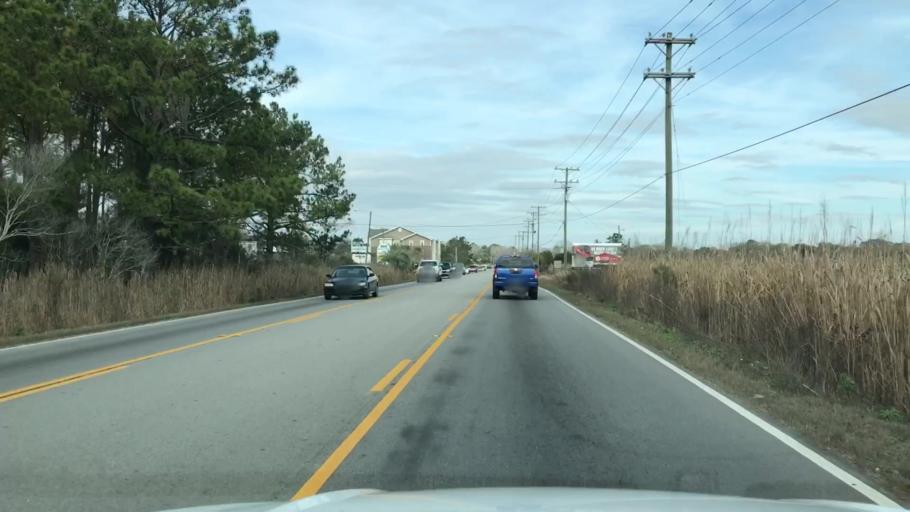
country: US
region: South Carolina
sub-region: Charleston County
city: Shell Point
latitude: 32.7974
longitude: -80.1086
